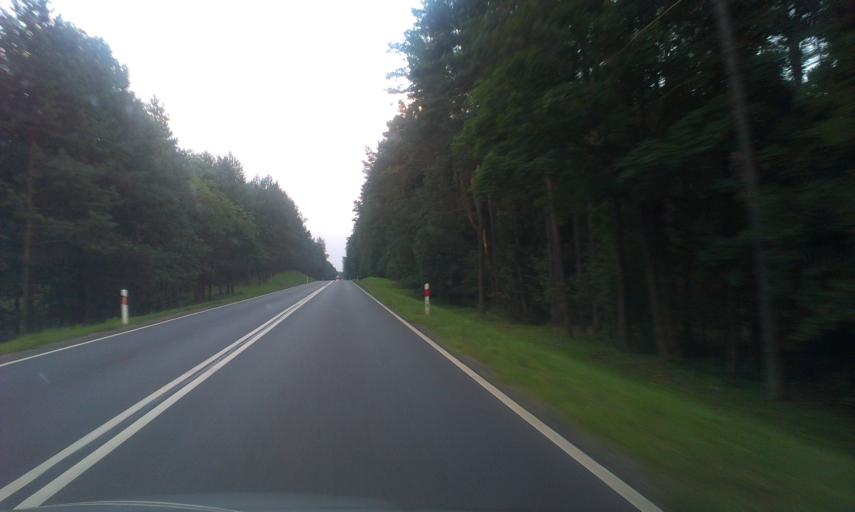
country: PL
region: West Pomeranian Voivodeship
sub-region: Powiat koszalinski
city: Sianow
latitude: 54.0885
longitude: 16.3731
